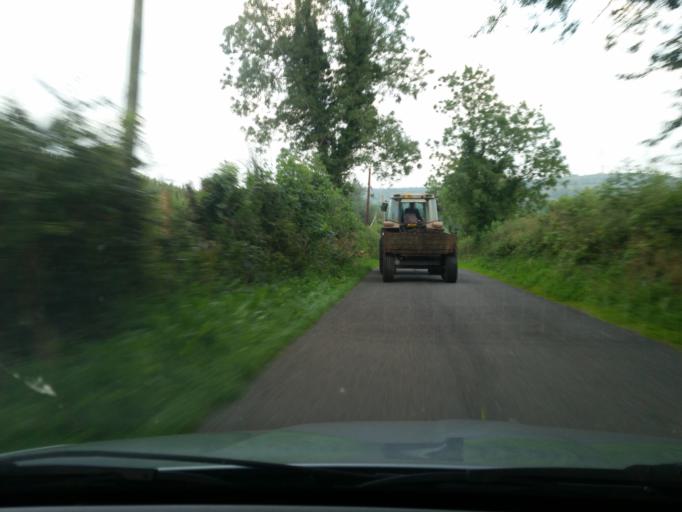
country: GB
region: Northern Ireland
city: Fivemiletown
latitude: 54.3709
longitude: -7.2962
